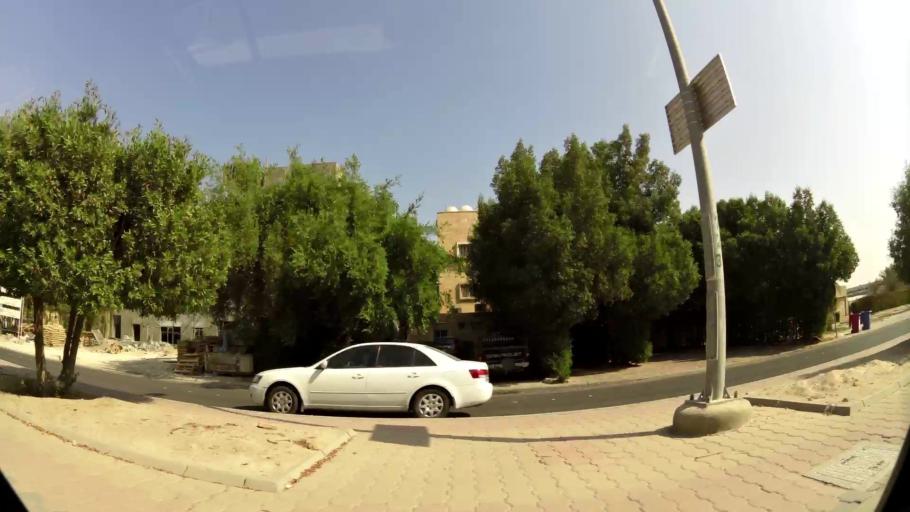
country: KW
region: Al Ahmadi
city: Al Fahahil
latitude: 29.0747
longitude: 48.1175
